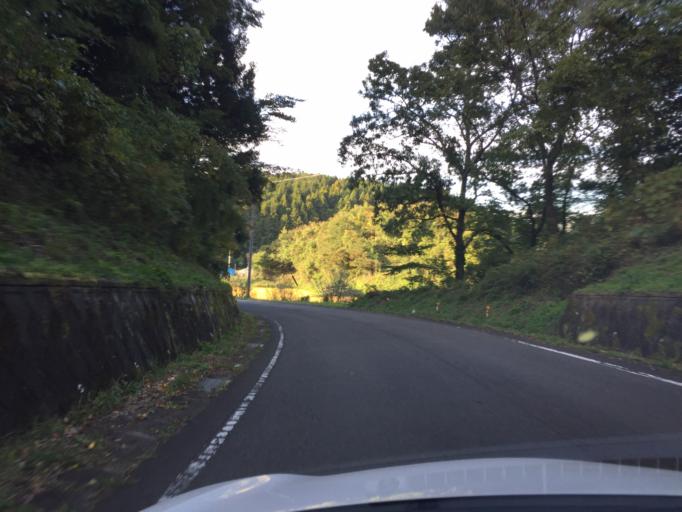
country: JP
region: Fukushima
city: Ishikawa
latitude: 37.2186
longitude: 140.5824
